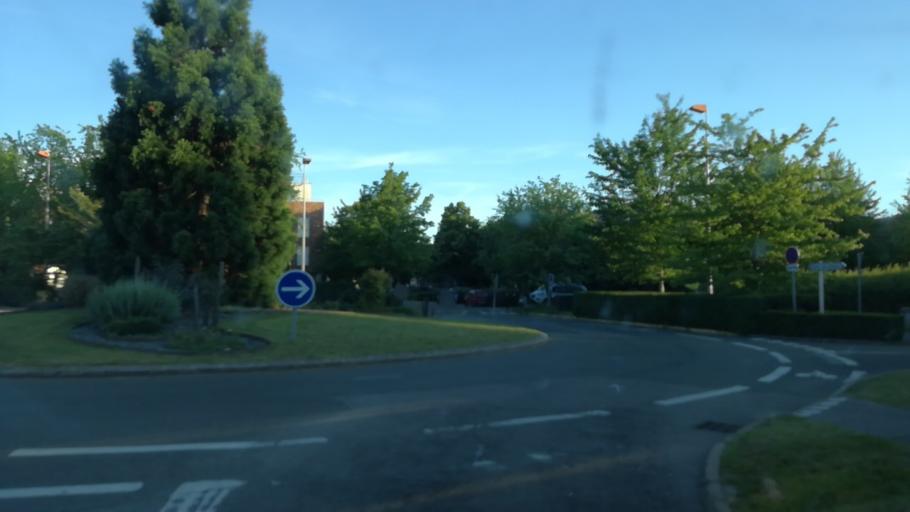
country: FR
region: Ile-de-France
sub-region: Departement des Yvelines
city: Elancourt
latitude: 48.7695
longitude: 1.9622
